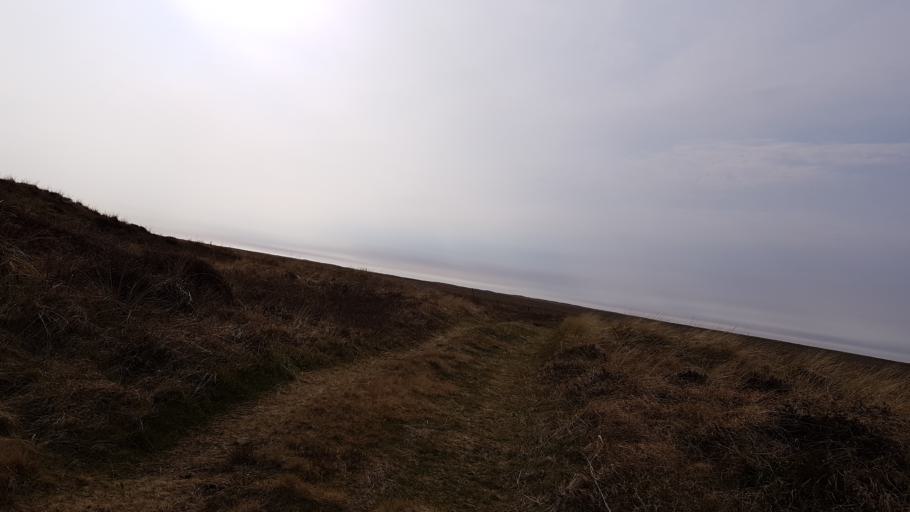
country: DE
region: Schleswig-Holstein
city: List
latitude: 55.1625
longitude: 8.5197
